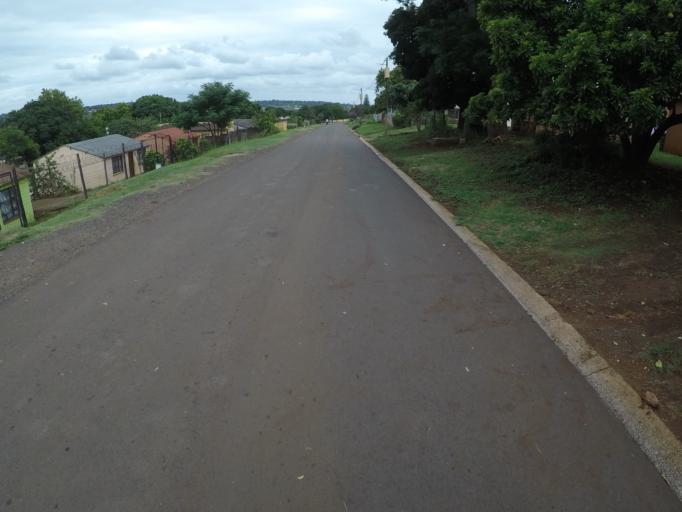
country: ZA
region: KwaZulu-Natal
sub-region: uThungulu District Municipality
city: Empangeni
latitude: -28.7672
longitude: 31.8606
